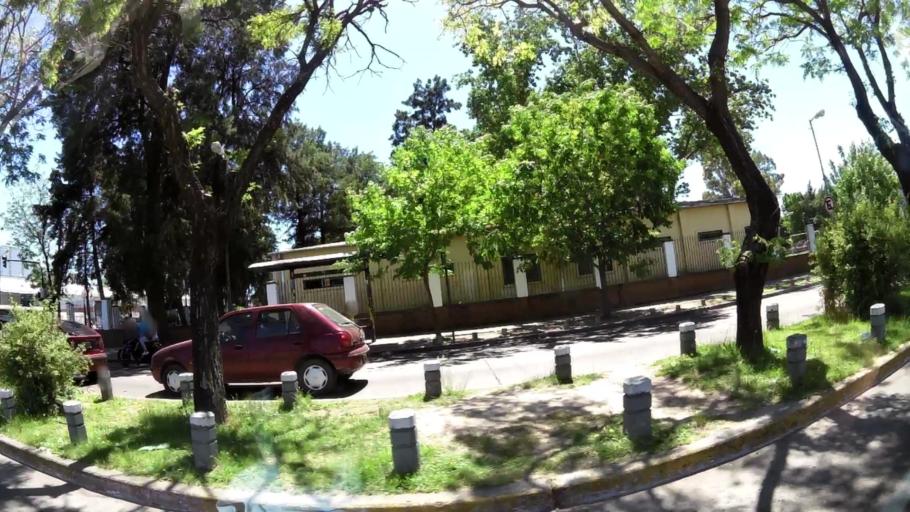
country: AR
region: Buenos Aires
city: Caseros
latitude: -34.5816
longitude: -58.5538
